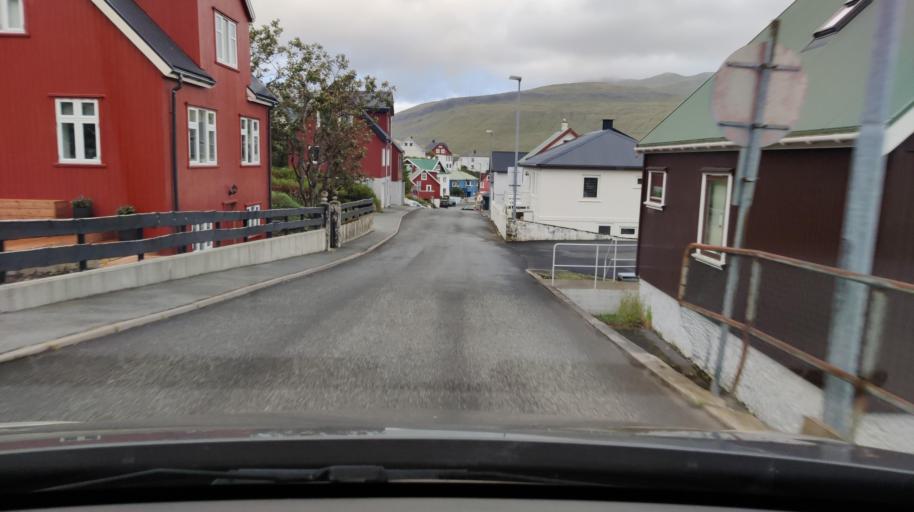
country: FO
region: Streymoy
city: Vestmanna
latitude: 62.1553
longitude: -7.1709
